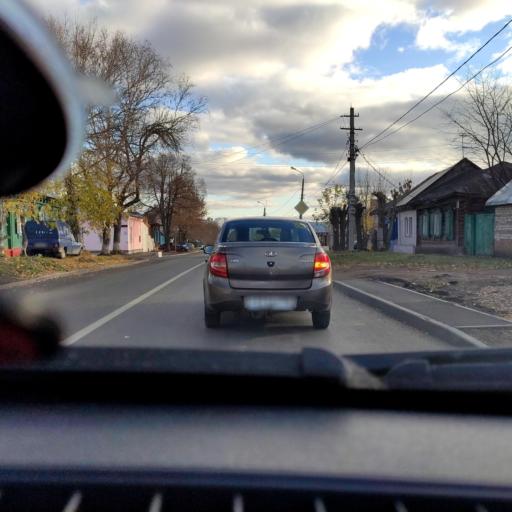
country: RU
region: Bashkortostan
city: Ufa
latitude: 54.7229
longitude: 55.9686
